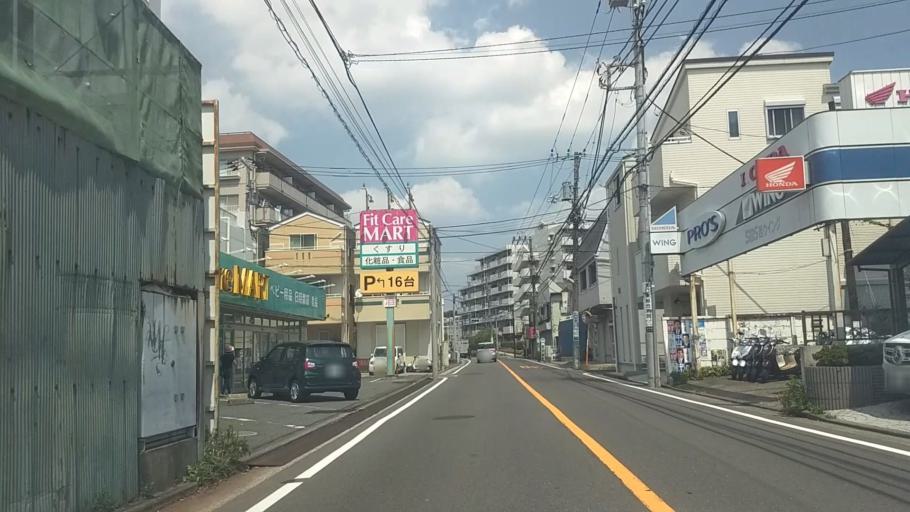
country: JP
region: Kanagawa
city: Yokohama
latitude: 35.4982
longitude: 139.6461
